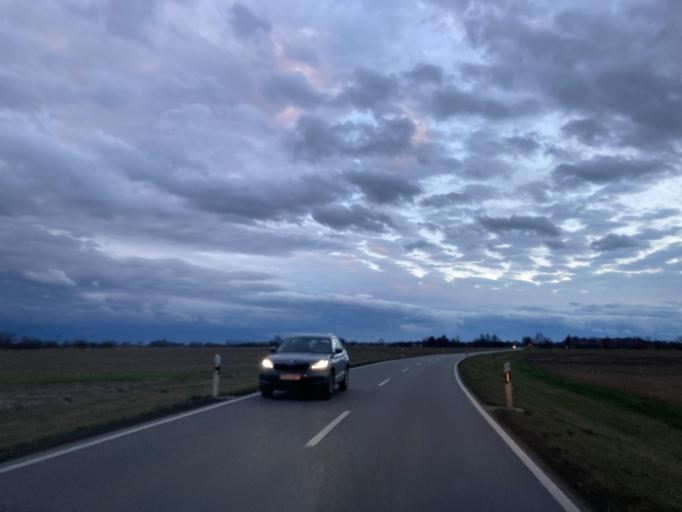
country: DE
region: Baden-Wuerttemberg
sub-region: Freiburg Region
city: Breisach am Rhein
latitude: 48.0588
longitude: 7.5937
